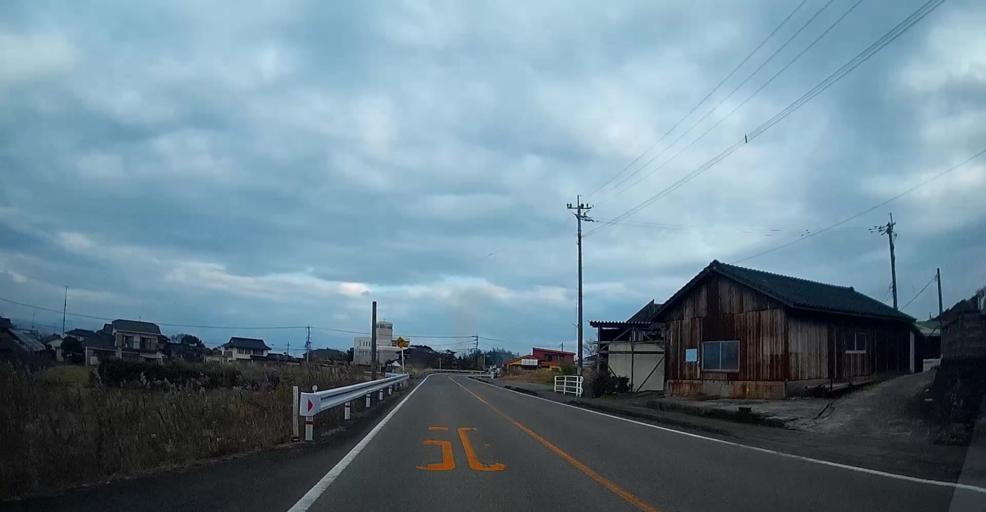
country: JP
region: Kumamoto
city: Hondo
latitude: 32.4756
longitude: 130.2604
